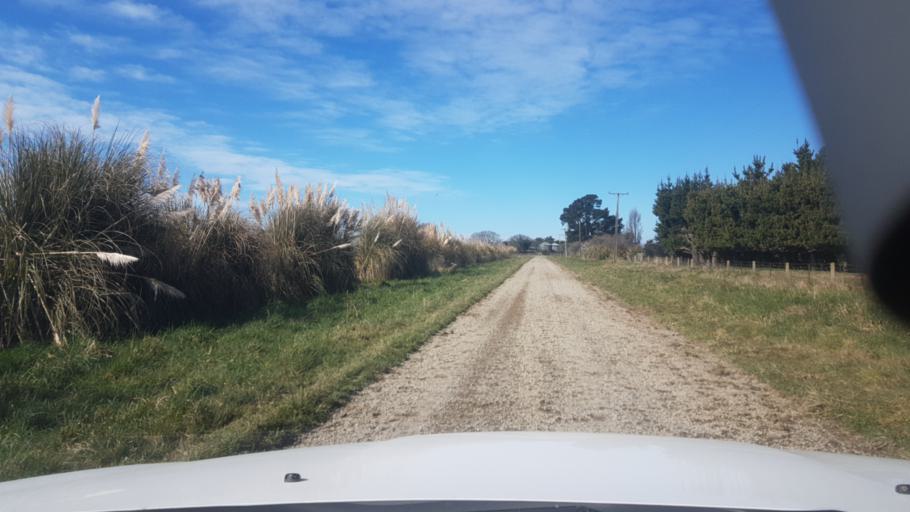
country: NZ
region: Canterbury
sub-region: Timaru District
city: Timaru
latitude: -44.2652
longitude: 171.3525
